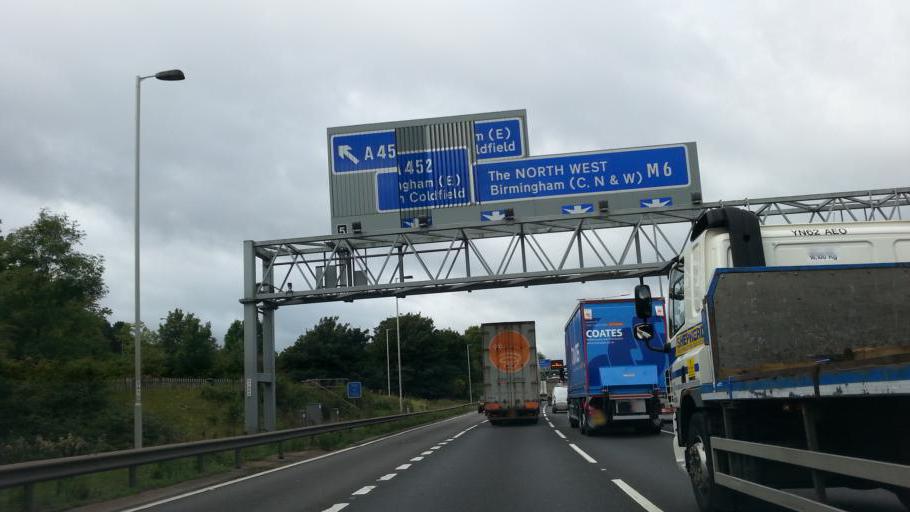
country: GB
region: England
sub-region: Warwickshire
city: Water Orton
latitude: 52.5097
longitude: -1.7853
